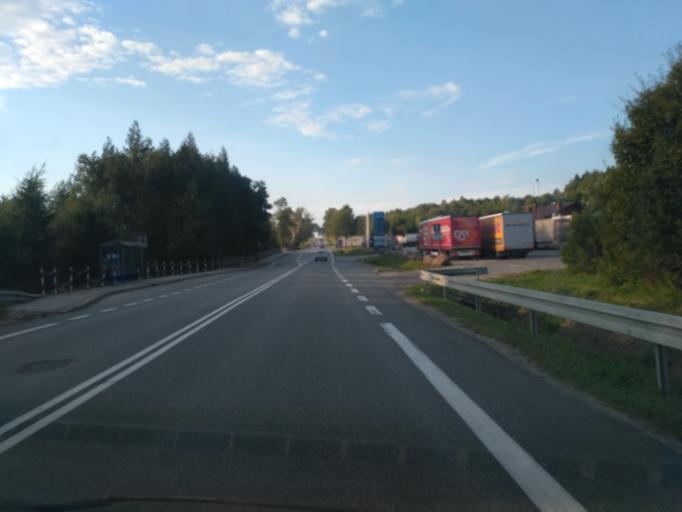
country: PL
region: Subcarpathian Voivodeship
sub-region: Powiat krosnienski
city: Dukla
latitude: 49.5791
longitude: 21.7030
